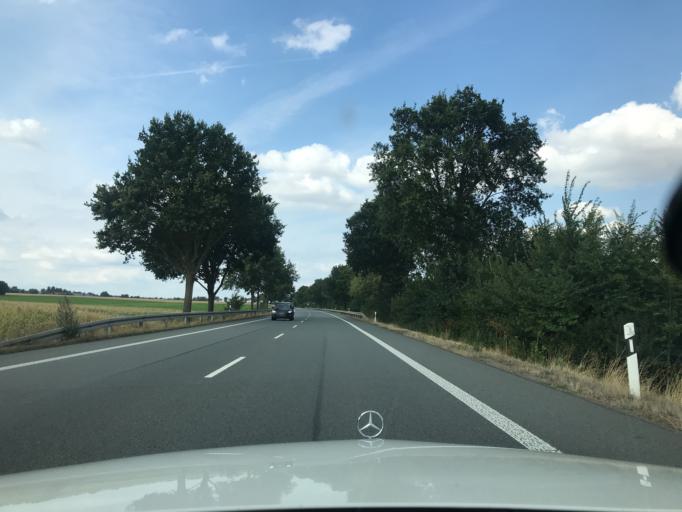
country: DE
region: North Rhine-Westphalia
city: Warburg
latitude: 51.5202
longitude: 9.1434
